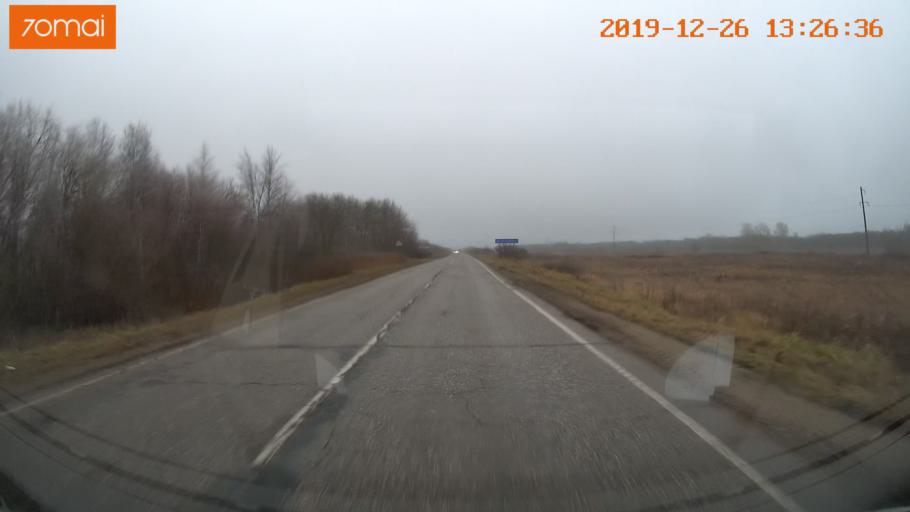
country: RU
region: Vologda
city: Cherepovets
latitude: 58.8622
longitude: 38.2288
